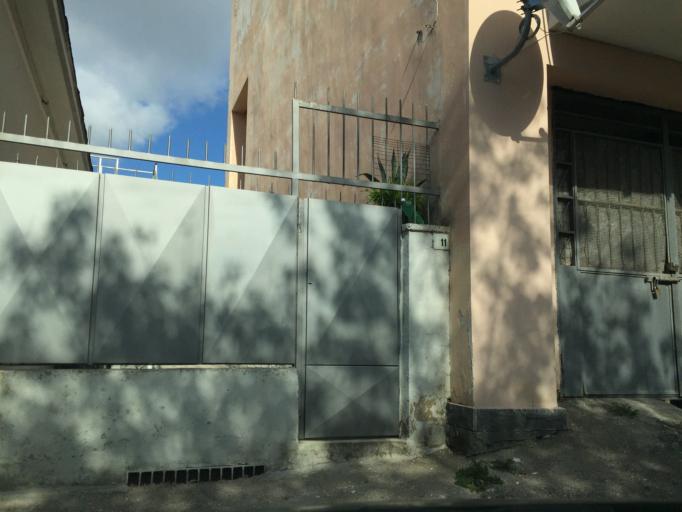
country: IT
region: Campania
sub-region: Provincia di Napoli
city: Massa di Somma
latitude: 40.8480
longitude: 14.3695
